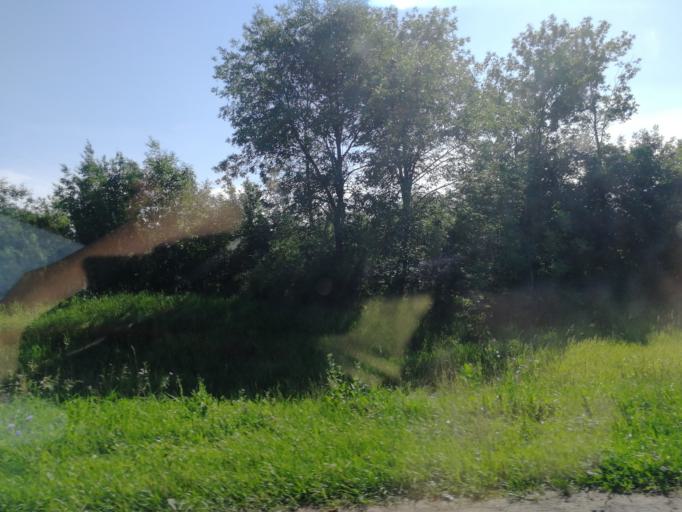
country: RU
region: Tula
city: Tovarkovskiy
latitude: 53.6272
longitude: 38.2530
